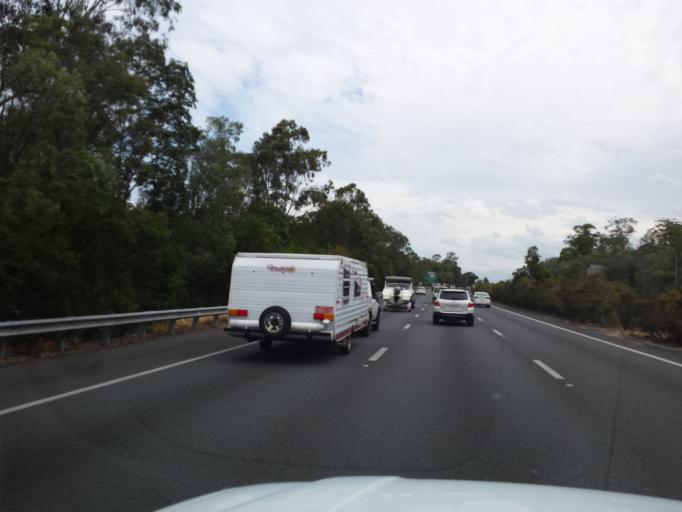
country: AU
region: Queensland
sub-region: Gold Coast
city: Nerang
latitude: -27.9652
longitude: 153.3462
